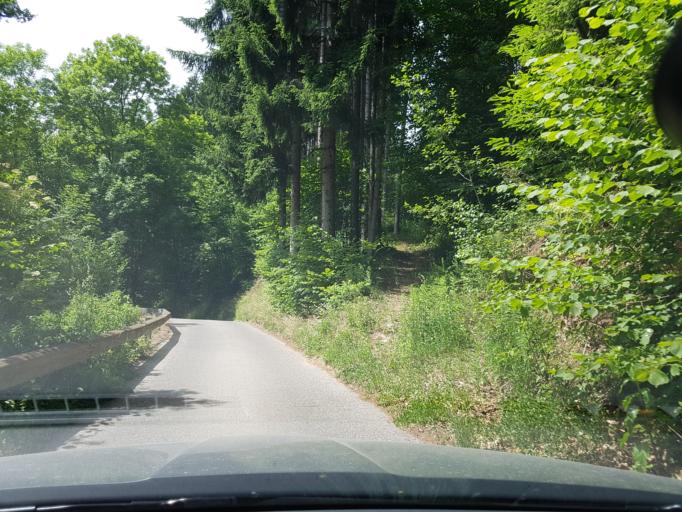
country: AT
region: Carinthia
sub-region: Politischer Bezirk Spittal an der Drau
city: Millstatt
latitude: 46.7782
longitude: 13.5540
